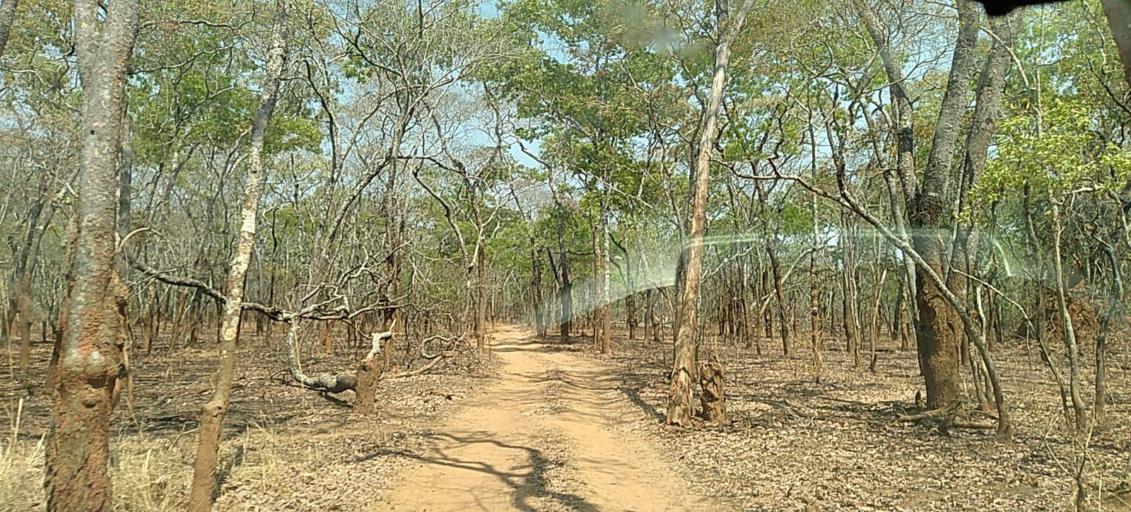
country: ZM
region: North-Western
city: Kasempa
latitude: -13.3935
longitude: 25.5977
